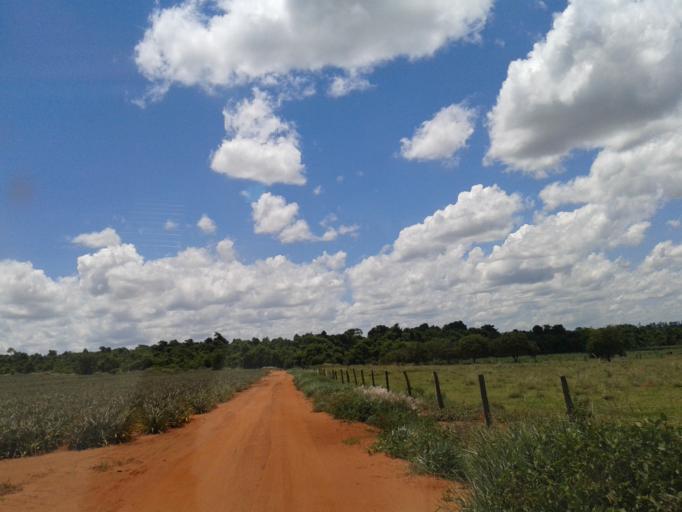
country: BR
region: Minas Gerais
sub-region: Centralina
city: Centralina
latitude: -18.6961
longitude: -49.1587
